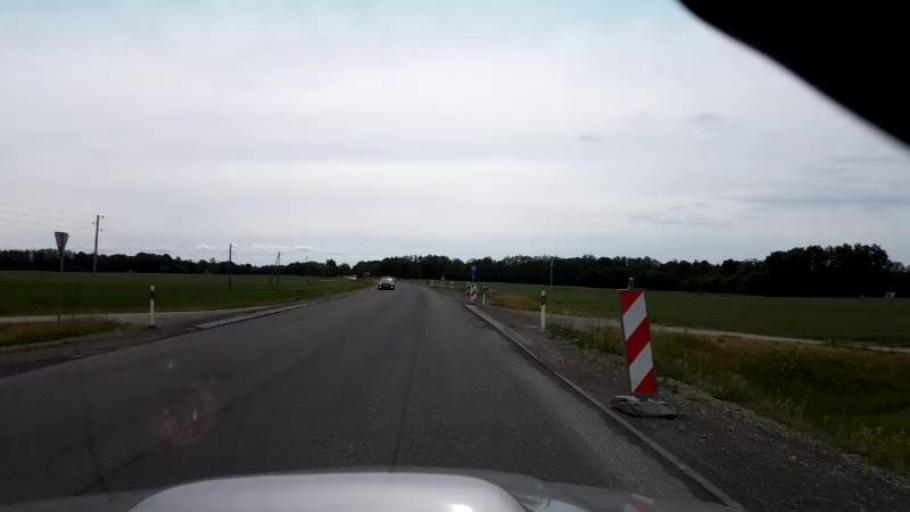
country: LV
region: Bauskas Rajons
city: Bauska
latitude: 56.3301
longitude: 24.3022
